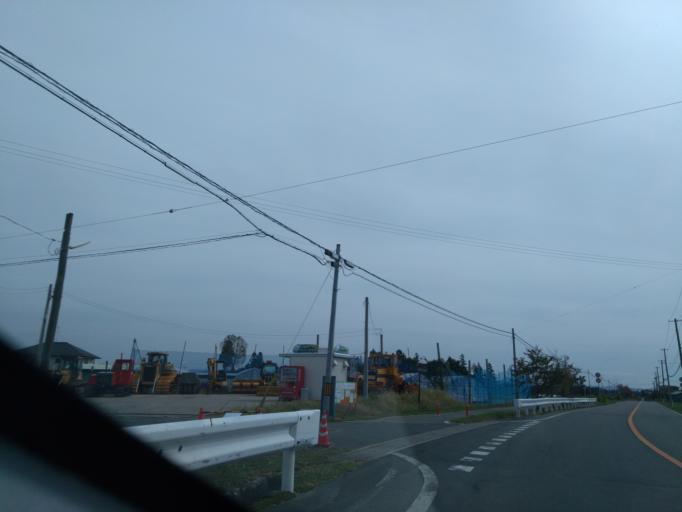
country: JP
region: Iwate
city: Hanamaki
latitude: 39.4345
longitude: 141.0823
